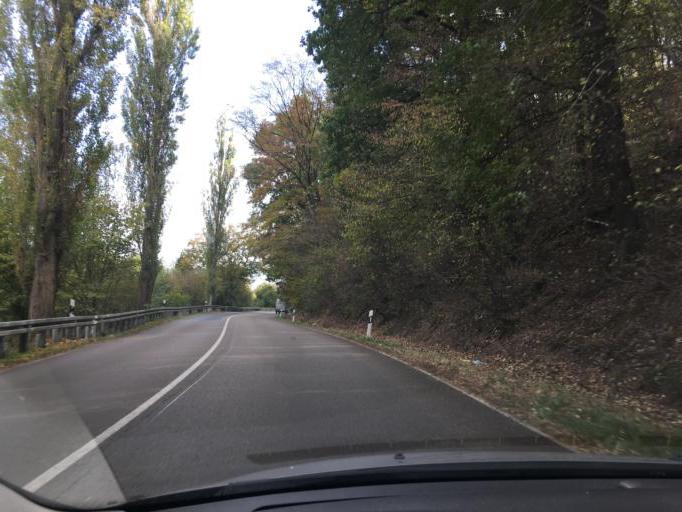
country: DE
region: Saxony
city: Meissen
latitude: 51.1966
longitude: 13.4098
